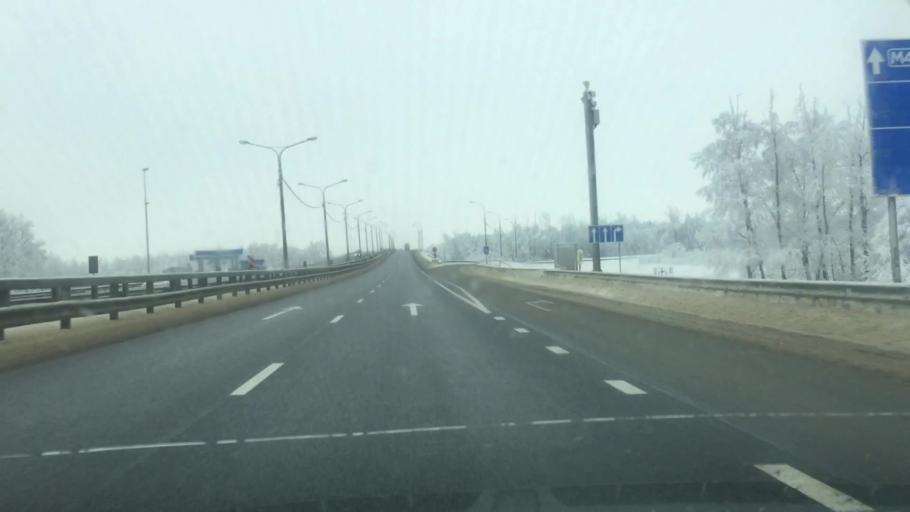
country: RU
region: Lipetsk
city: Yelets
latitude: 52.5528
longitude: 38.7166
